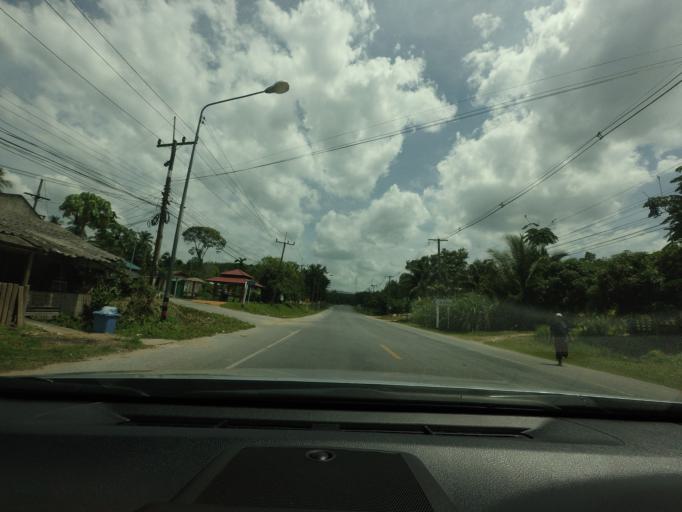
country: TH
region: Yala
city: Raman
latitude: 6.4691
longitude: 101.3923
